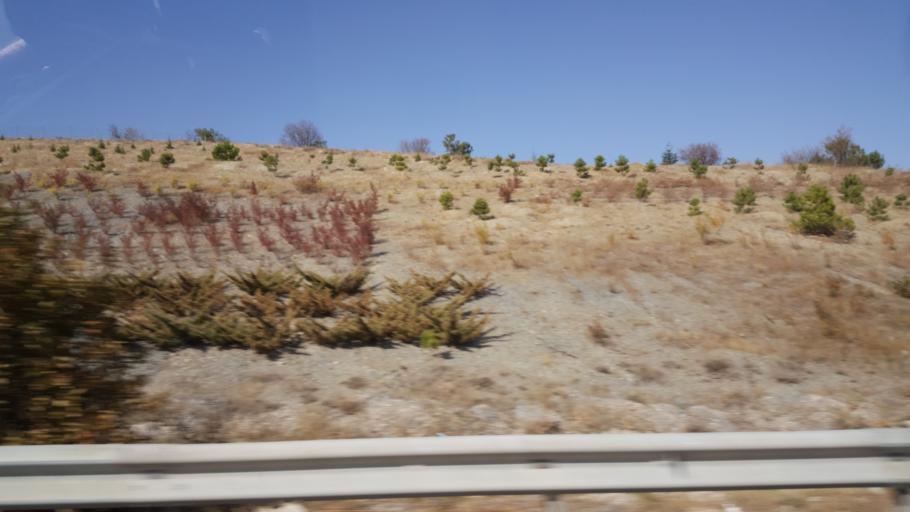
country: TR
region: Ankara
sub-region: Goelbasi
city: Golbasi
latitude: 39.8127
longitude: 32.8067
